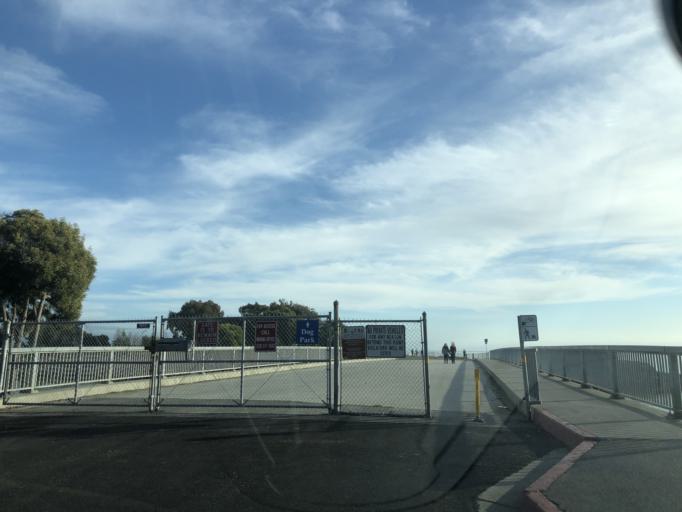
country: US
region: California
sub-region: Alameda County
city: San Leandro
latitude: 37.6915
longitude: -122.1838
